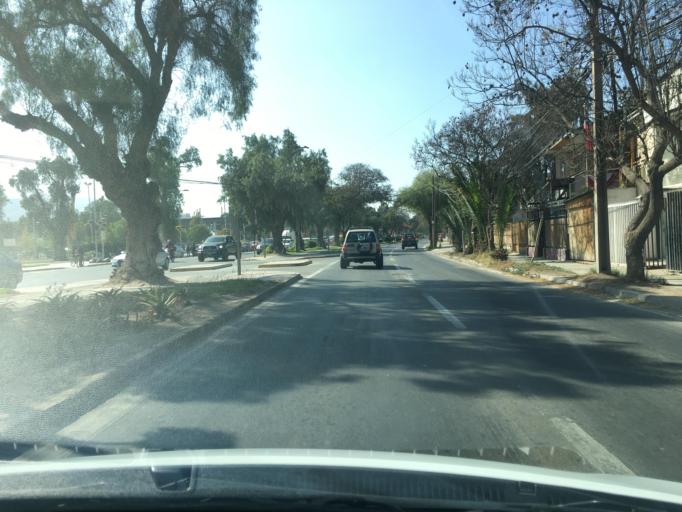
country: CL
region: Atacama
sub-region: Provincia de Copiapo
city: Copiapo
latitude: -27.3763
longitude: -70.3234
